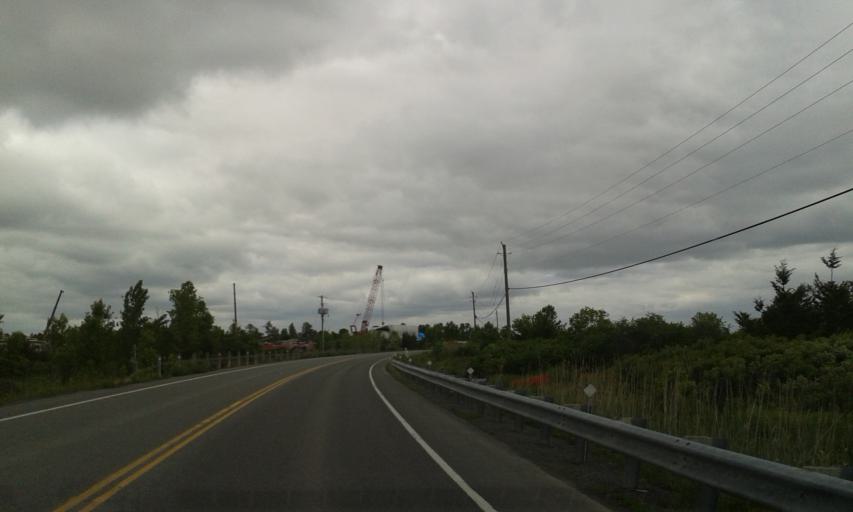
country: CA
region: Ontario
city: Skatepark
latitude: 44.1495
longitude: -76.8382
